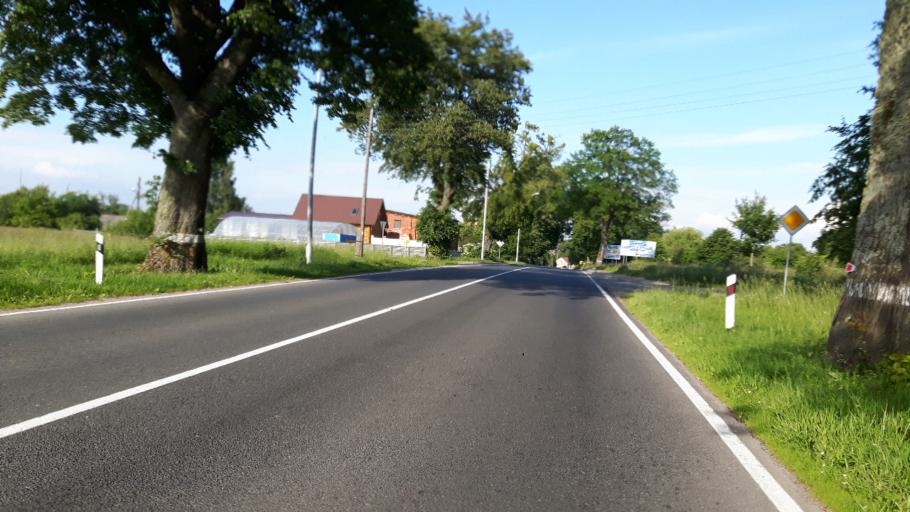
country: RU
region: Kaliningrad
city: Ladushkin
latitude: 54.5003
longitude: 20.0890
